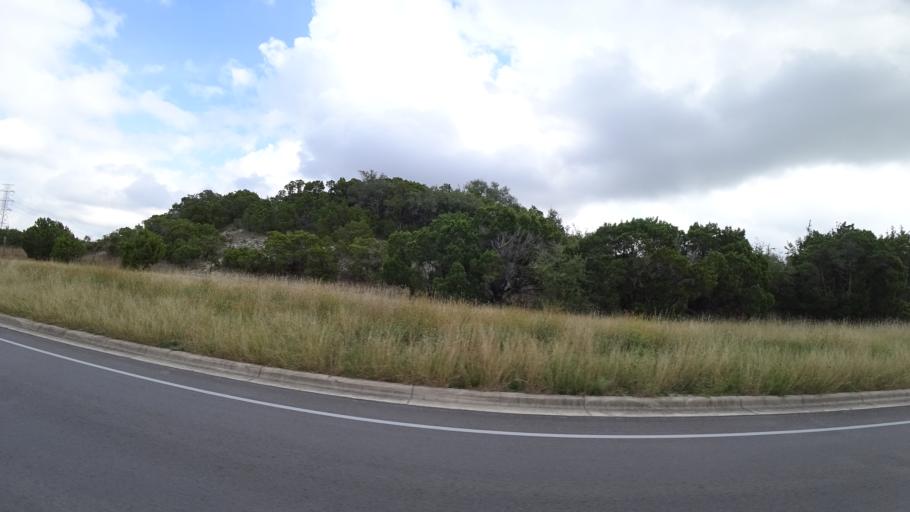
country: US
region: Texas
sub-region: Travis County
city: Hudson Bend
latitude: 30.3867
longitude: -97.8708
